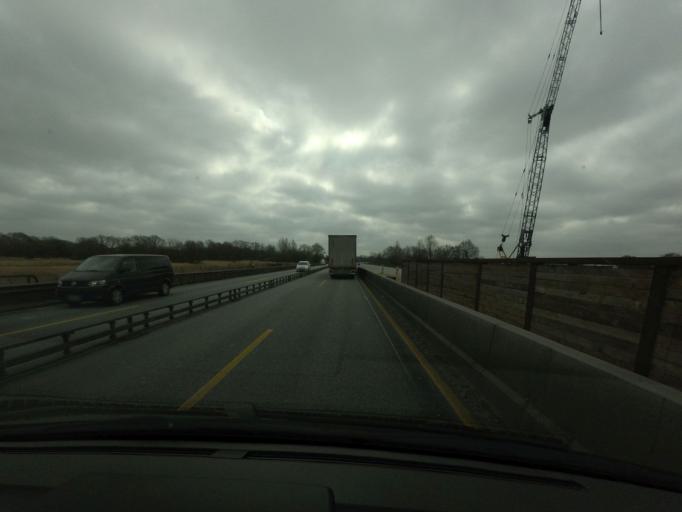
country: DE
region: Schleswig-Holstein
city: Alveslohe
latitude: 53.8092
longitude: 9.9264
